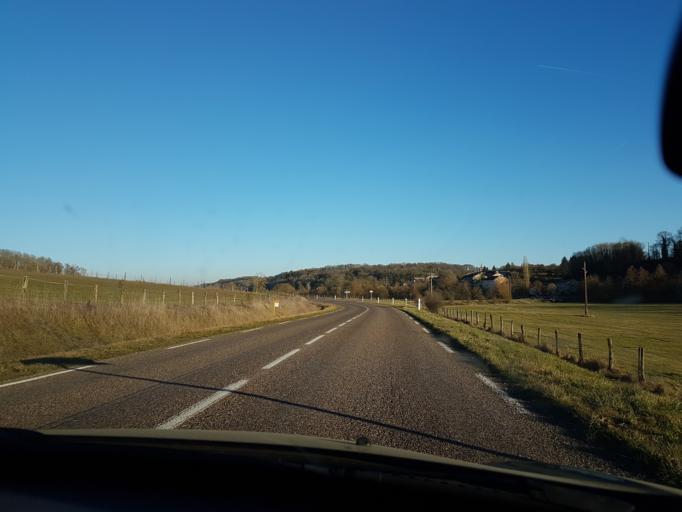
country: FR
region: Champagne-Ardenne
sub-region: Departement de la Haute-Marne
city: Bourbonne-les-Bains
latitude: 47.9399
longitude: 5.7820
